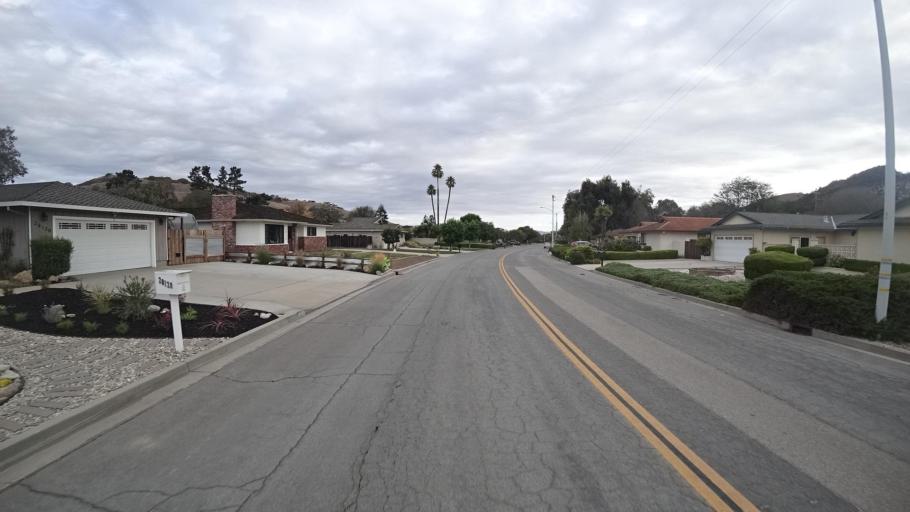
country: US
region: California
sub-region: Monterey County
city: Salinas
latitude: 36.6129
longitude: -121.6911
